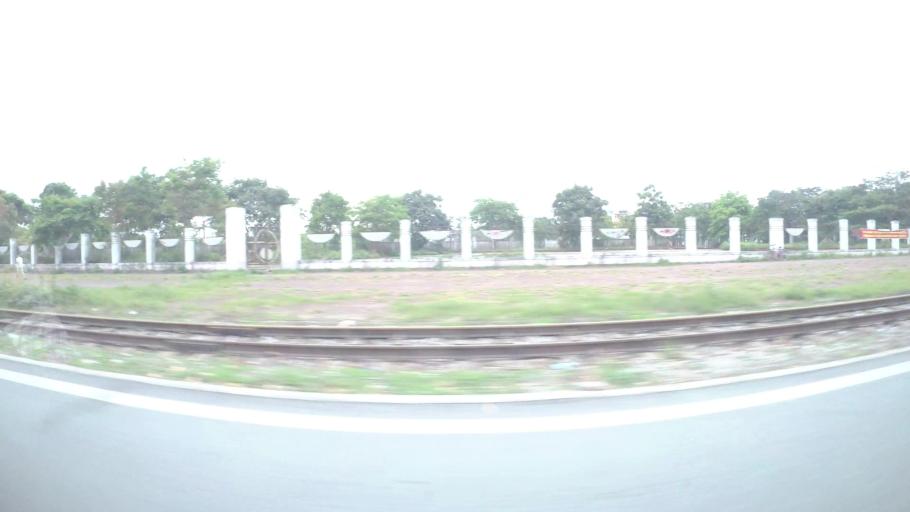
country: VN
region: Ha Noi
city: Hoan Kiem
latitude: 21.0611
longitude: 105.8904
